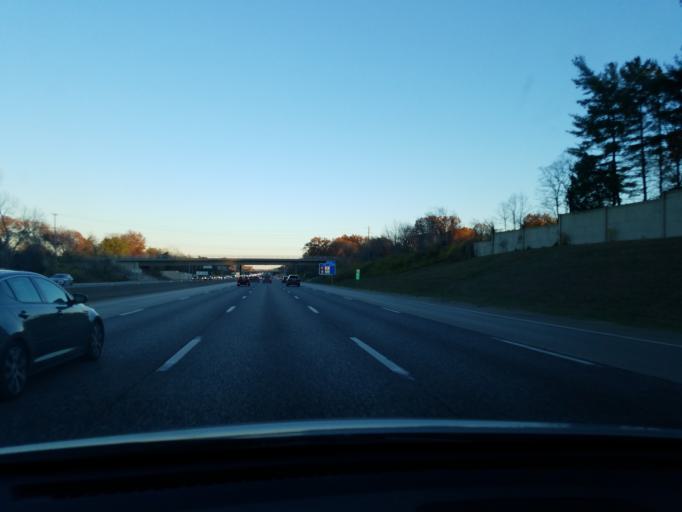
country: US
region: Missouri
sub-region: Saint Louis County
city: Sappington
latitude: 38.5160
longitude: -90.3825
